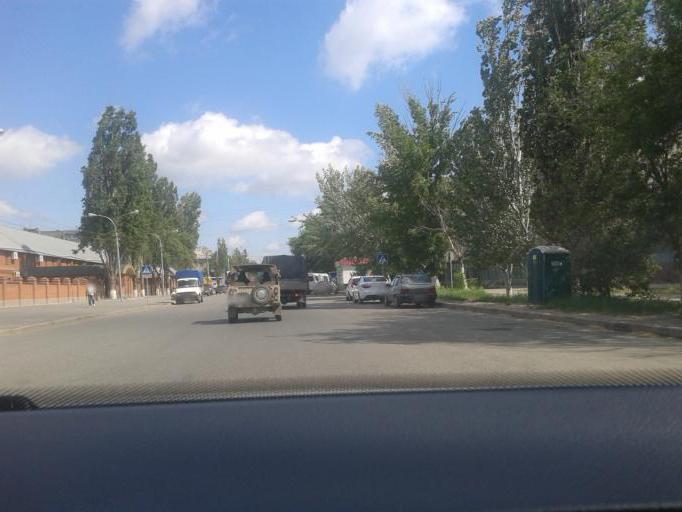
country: RU
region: Volgograd
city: Gorodishche
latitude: 48.7656
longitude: 44.4783
